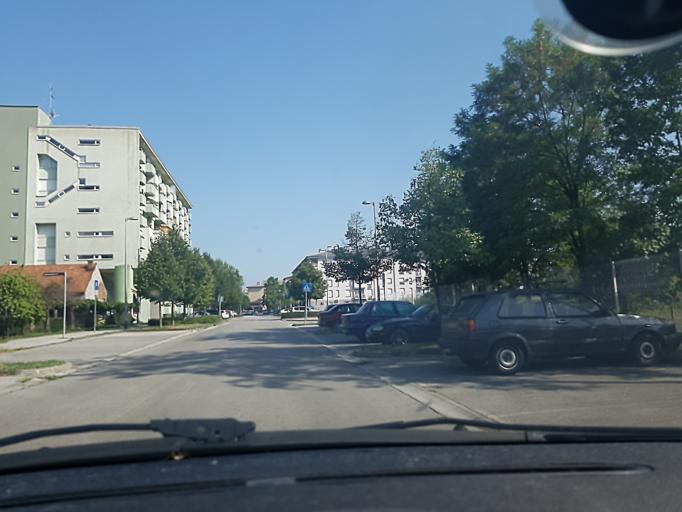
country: HR
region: Grad Zagreb
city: Jankomir
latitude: 45.7947
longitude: 15.9129
